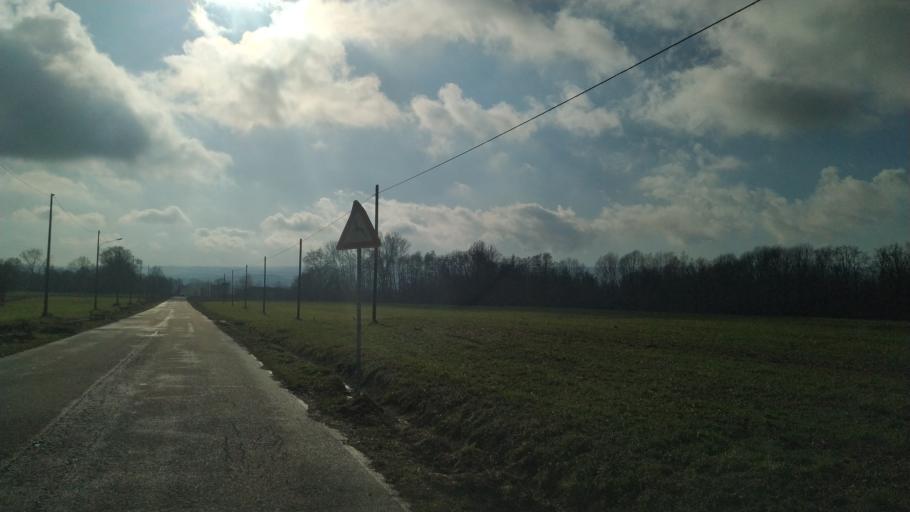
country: IT
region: Piedmont
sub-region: Provincia di Biella
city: Occhieppo Inferiore
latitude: 45.5417
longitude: 8.0252
